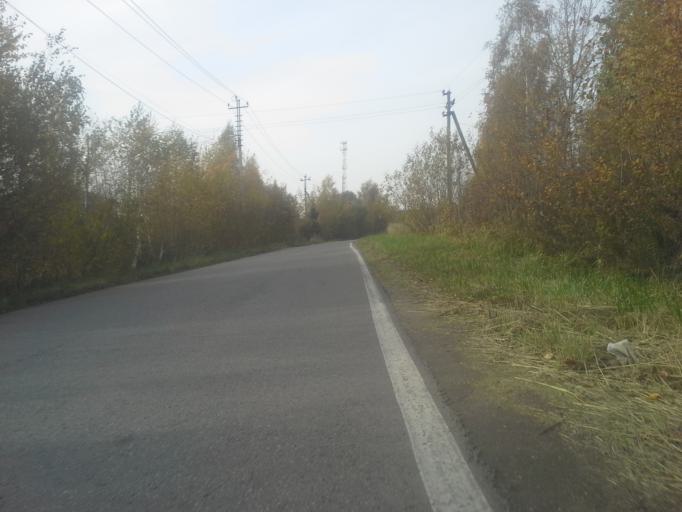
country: RU
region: Moskovskaya
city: Aprelevka
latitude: 55.5594
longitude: 37.0469
